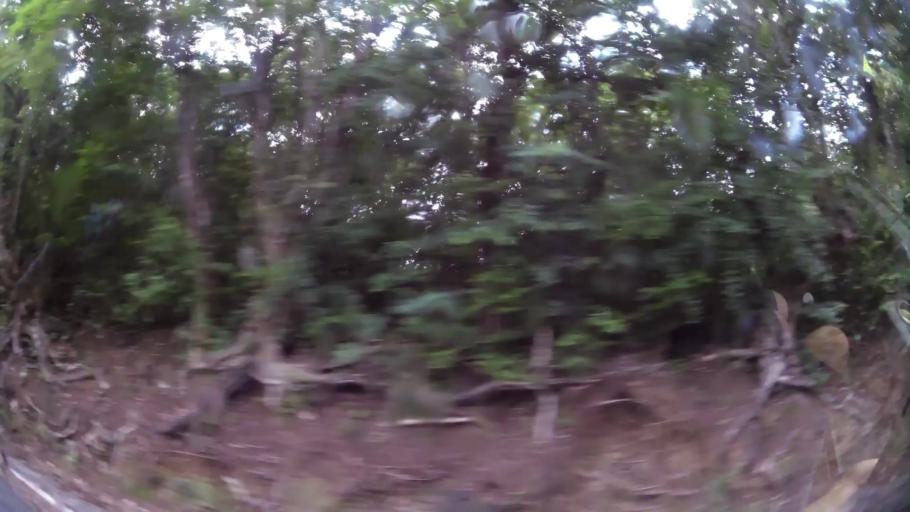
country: DM
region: Saint George
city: Roseau
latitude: 15.3276
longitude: -61.3921
